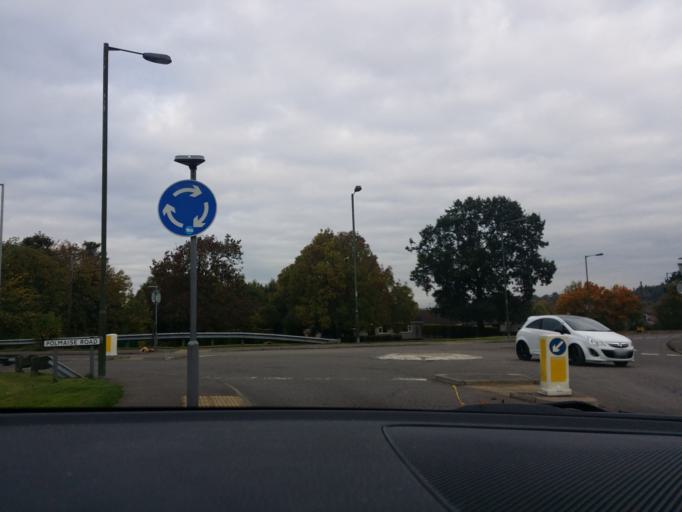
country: GB
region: Scotland
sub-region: Stirling
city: Stirling
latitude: 56.1053
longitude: -3.9552
